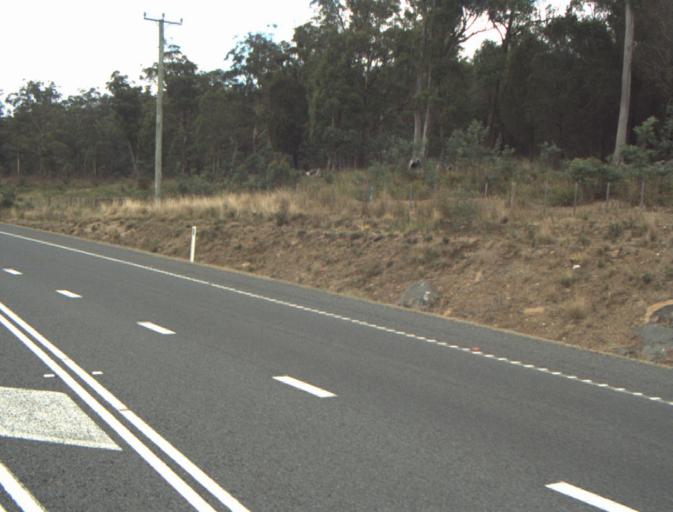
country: AU
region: Tasmania
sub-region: Launceston
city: Mayfield
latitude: -41.2672
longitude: 147.0336
